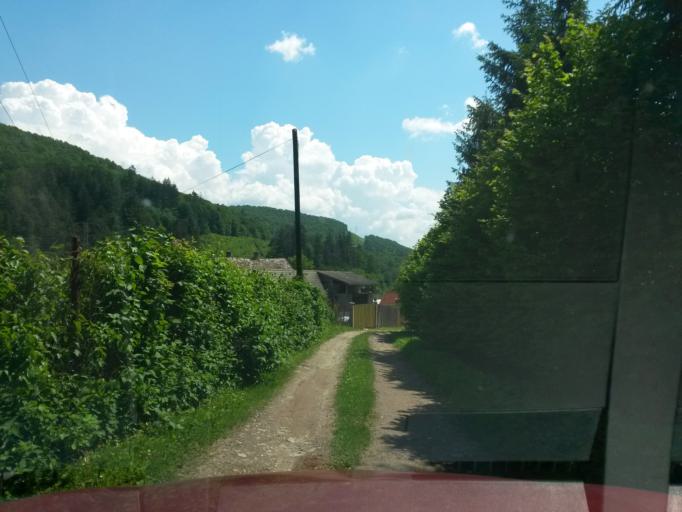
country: SK
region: Kosicky
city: Roznava
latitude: 48.6842
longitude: 20.5412
